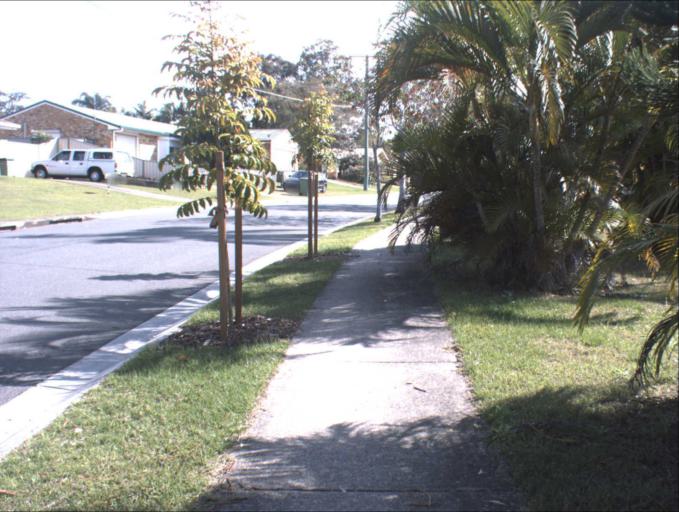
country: AU
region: Queensland
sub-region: Logan
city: Park Ridge South
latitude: -27.6941
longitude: 153.0154
